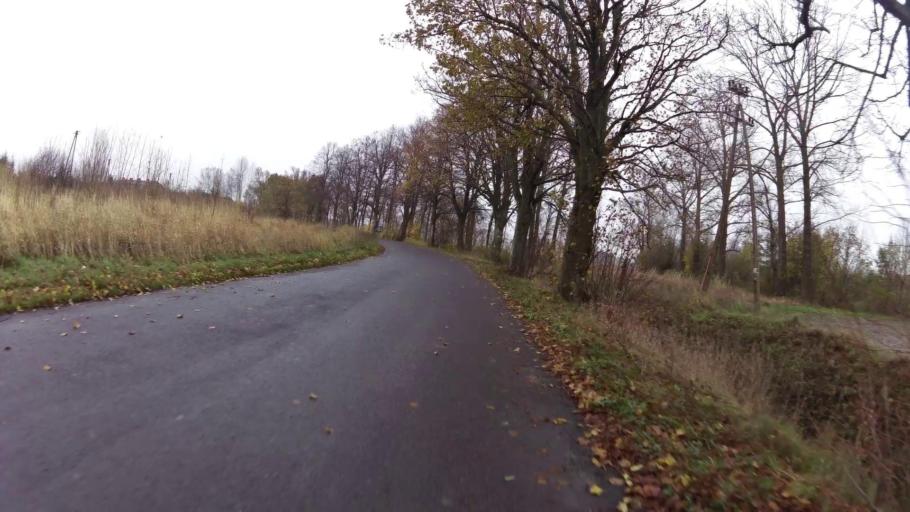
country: PL
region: West Pomeranian Voivodeship
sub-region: Powiat koszalinski
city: Mielno
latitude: 54.2391
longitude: 16.1058
